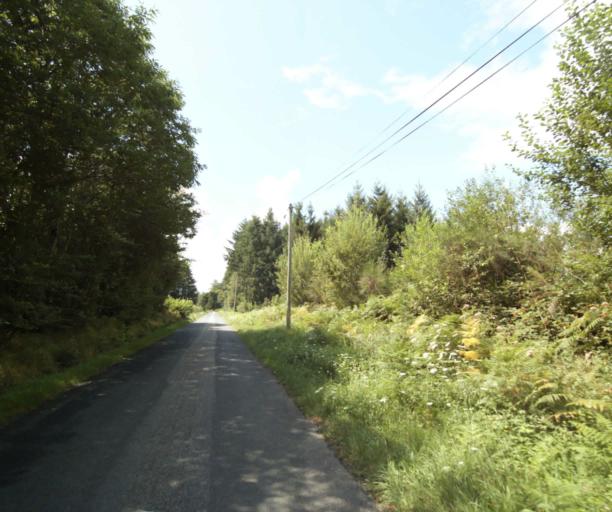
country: FR
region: Limousin
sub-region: Departement de la Correze
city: Sainte-Fortunade
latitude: 45.1786
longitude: 1.8360
